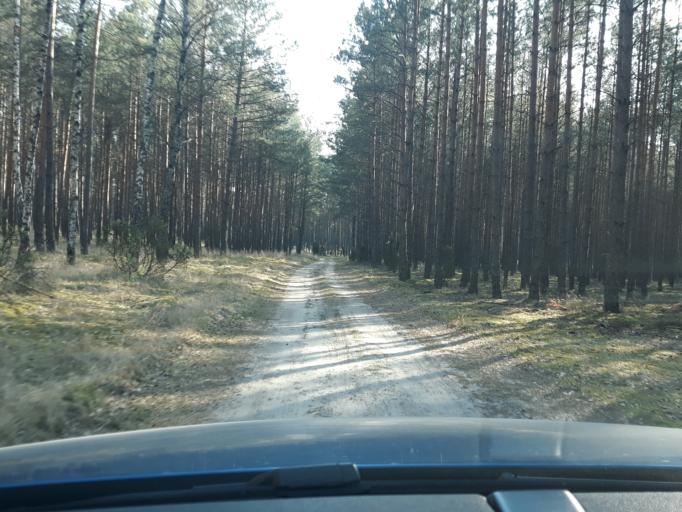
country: PL
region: Pomeranian Voivodeship
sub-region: Powiat bytowski
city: Lipnica
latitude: 53.9065
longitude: 17.4961
